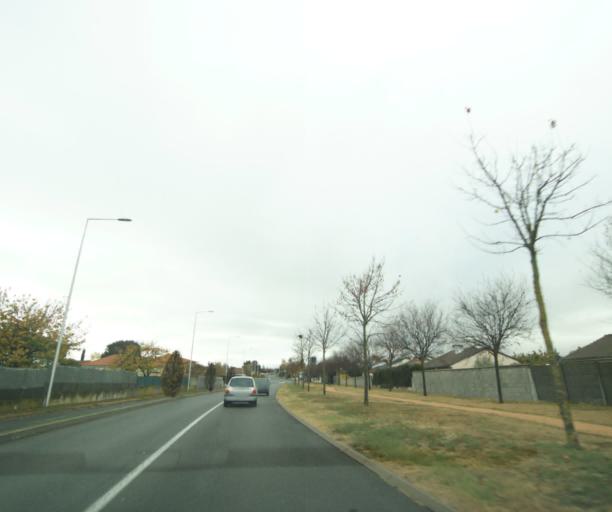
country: FR
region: Auvergne
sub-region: Departement du Puy-de-Dome
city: Cournon-d'Auvergne
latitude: 45.7349
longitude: 3.2135
